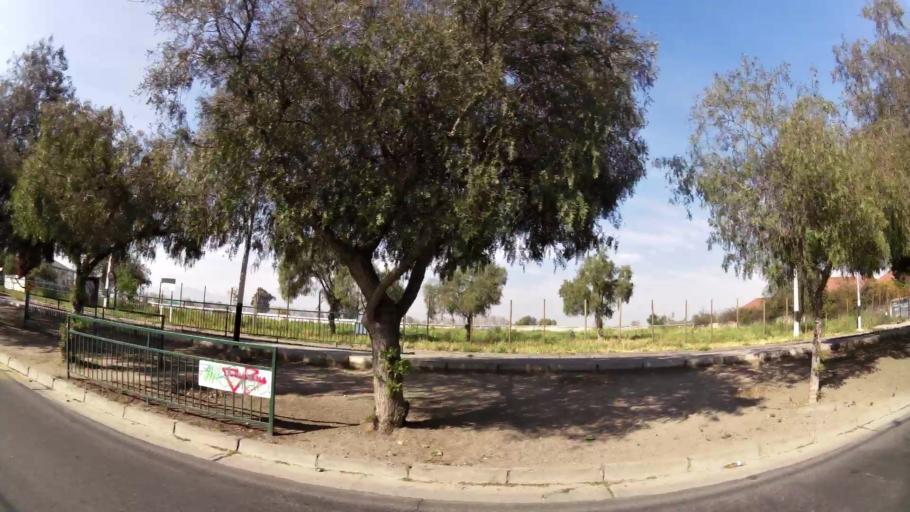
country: CL
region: Santiago Metropolitan
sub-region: Provincia de Santiago
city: La Pintana
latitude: -33.5641
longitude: -70.6434
